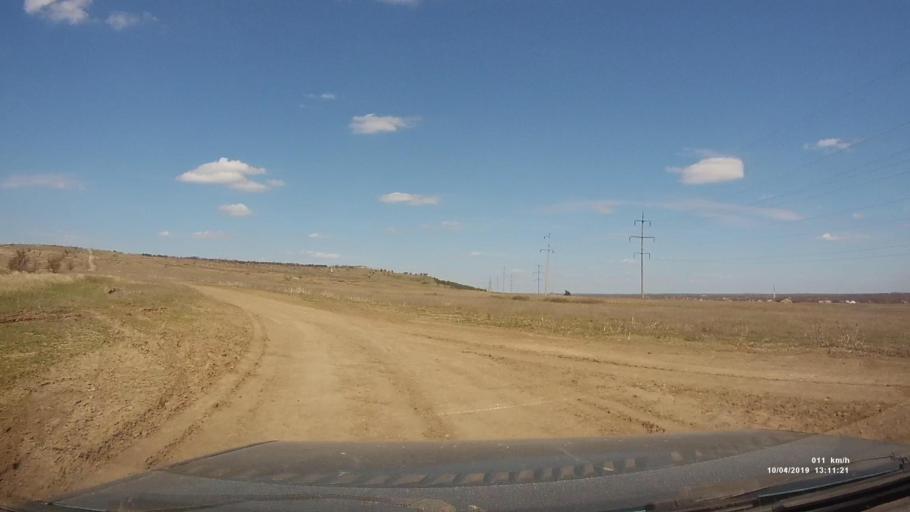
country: RU
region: Rostov
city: Masalovka
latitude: 48.4113
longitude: 40.2491
